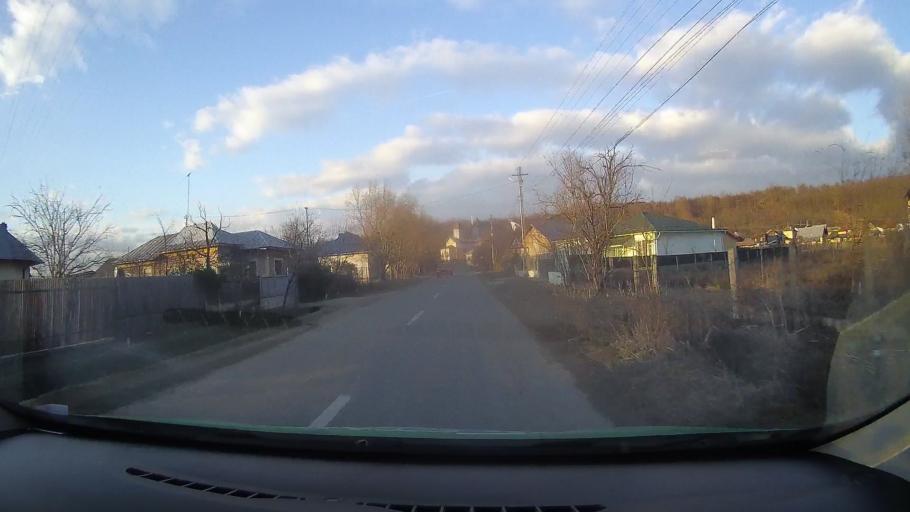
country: RO
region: Dambovita
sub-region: Comuna Gura Ocnitei
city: Adanca
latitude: 44.9170
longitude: 25.6160
